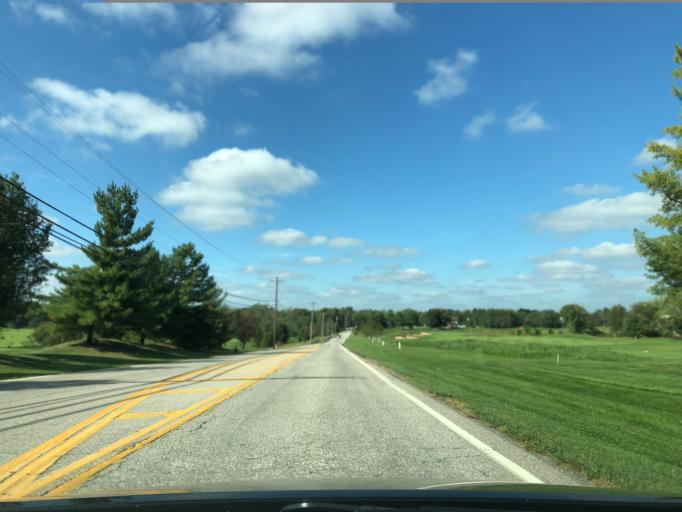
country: US
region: Ohio
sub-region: Hamilton County
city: Loveland
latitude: 39.2402
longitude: -84.2467
